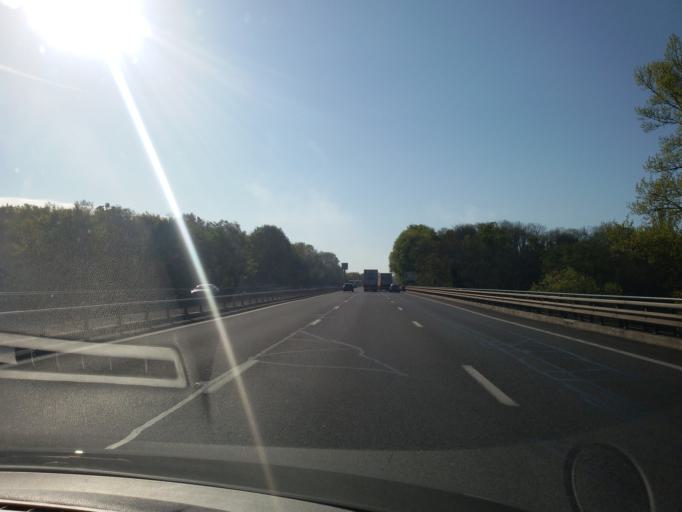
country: FR
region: Ile-de-France
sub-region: Departement de Seine-et-Marne
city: Nemours
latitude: 48.2870
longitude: 2.6908
